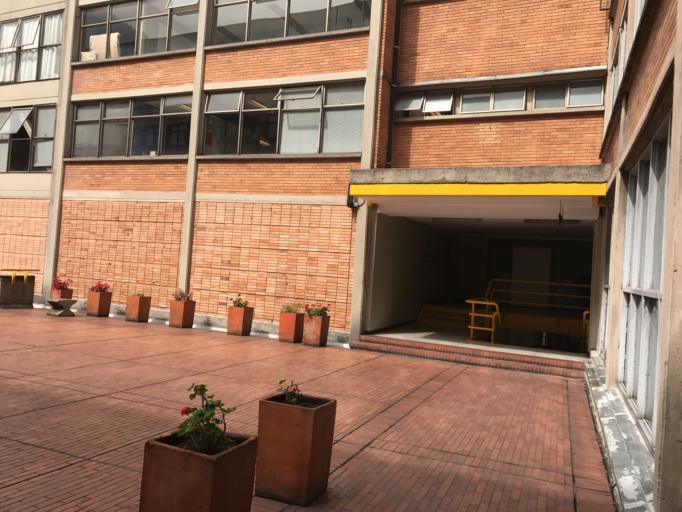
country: CO
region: Bogota D.C.
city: Bogota
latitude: 4.6071
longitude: -74.0678
